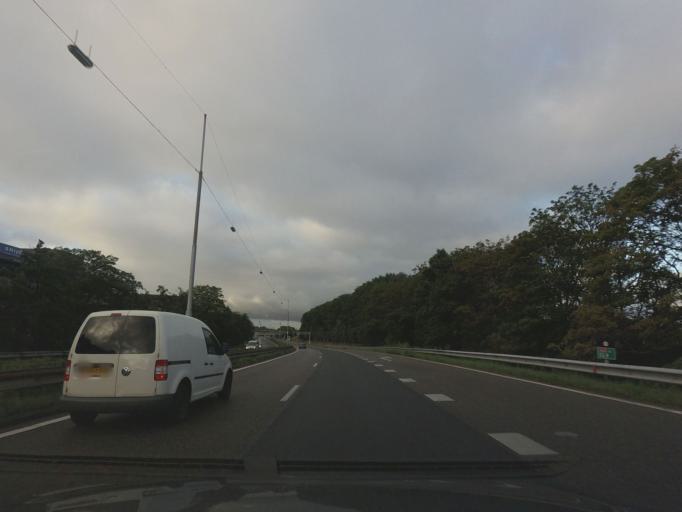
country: NL
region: North Holland
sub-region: Gemeente Beverwijk
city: Beverwijk
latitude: 52.4789
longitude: 4.6587
